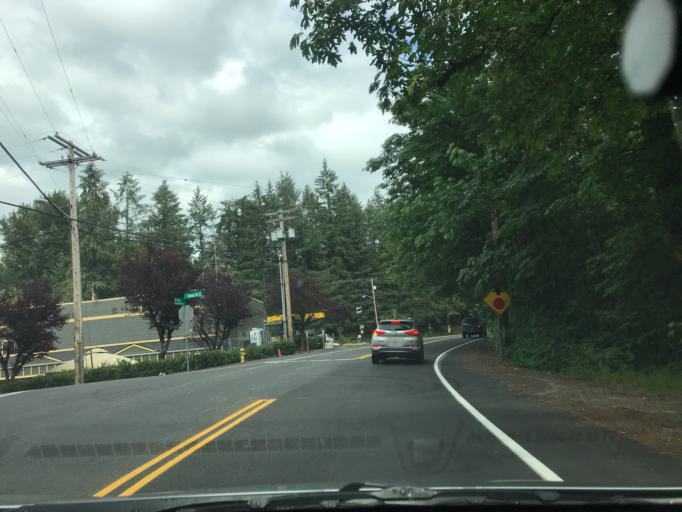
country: US
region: Washington
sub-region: King County
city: Lake Morton-Berrydale
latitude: 47.3122
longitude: -122.0966
